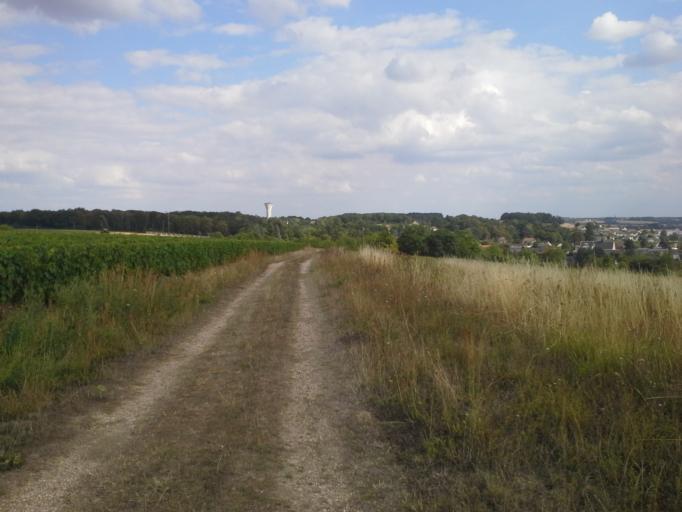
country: FR
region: Centre
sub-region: Departement du Loir-et-Cher
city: Villiers-sur-Loir
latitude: 47.8113
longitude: 0.9872
